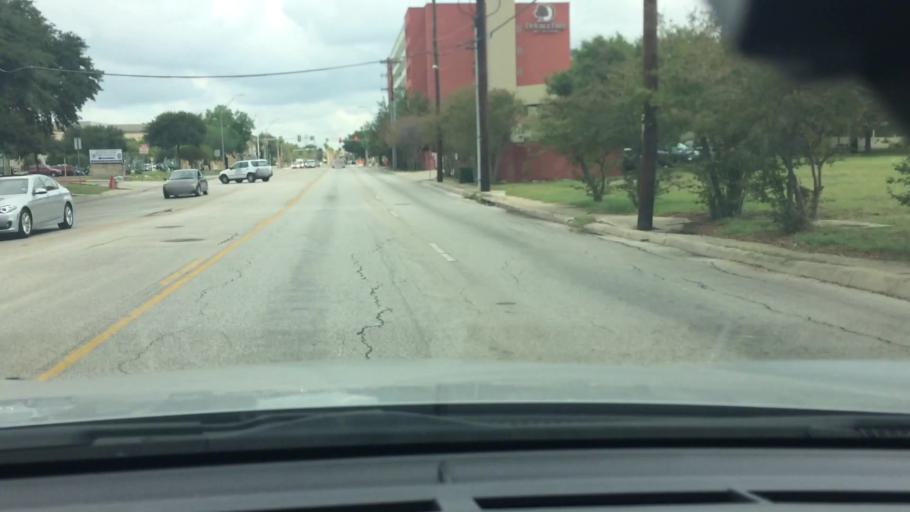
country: US
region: Texas
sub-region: Bexar County
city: San Antonio
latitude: 29.4211
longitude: -98.5045
